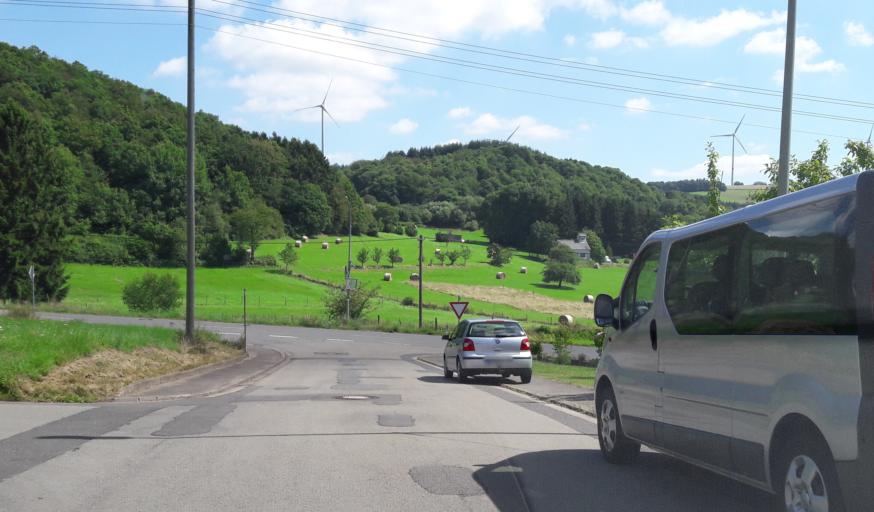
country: DE
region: Saarland
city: Freisen
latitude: 49.5576
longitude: 7.2441
